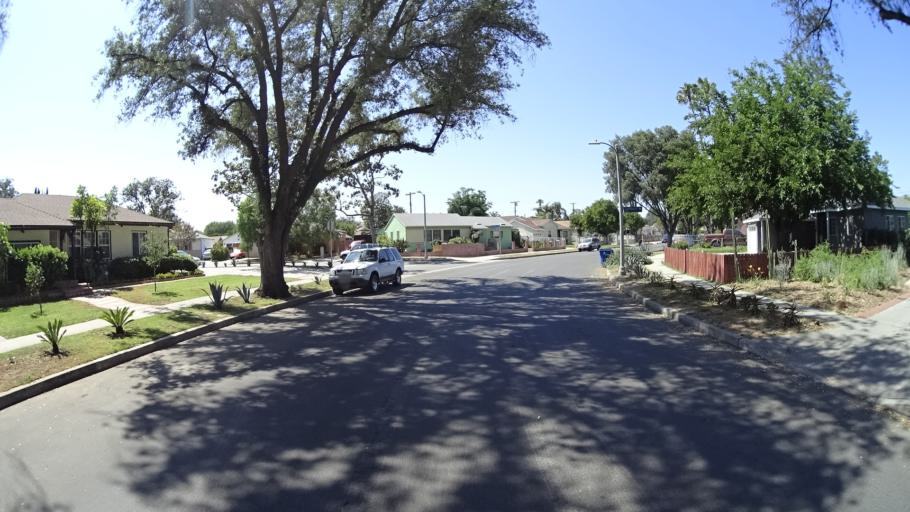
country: US
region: California
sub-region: Los Angeles County
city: Van Nuys
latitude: 34.2188
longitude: -118.4399
